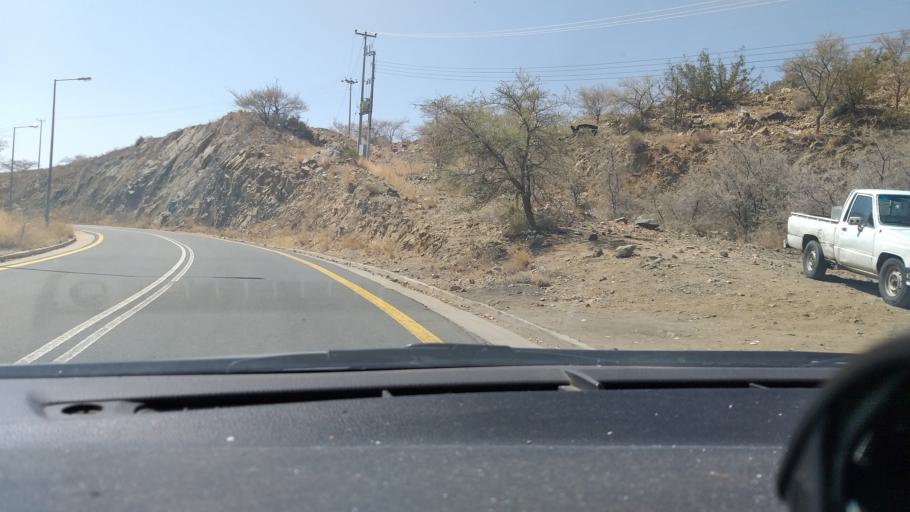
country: SA
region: Makkah
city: Ash Shafa
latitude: 21.1038
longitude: 40.3364
